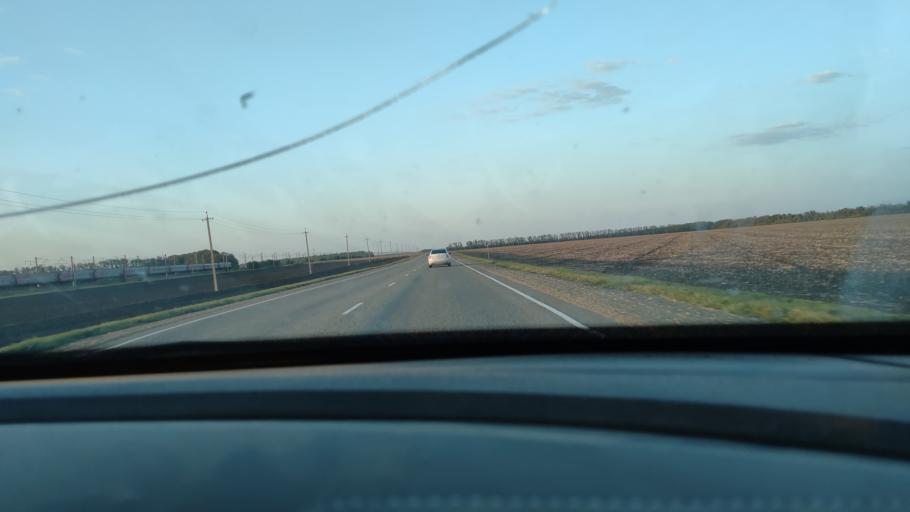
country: RU
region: Krasnodarskiy
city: Novominskaya
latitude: 46.3658
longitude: 38.9719
